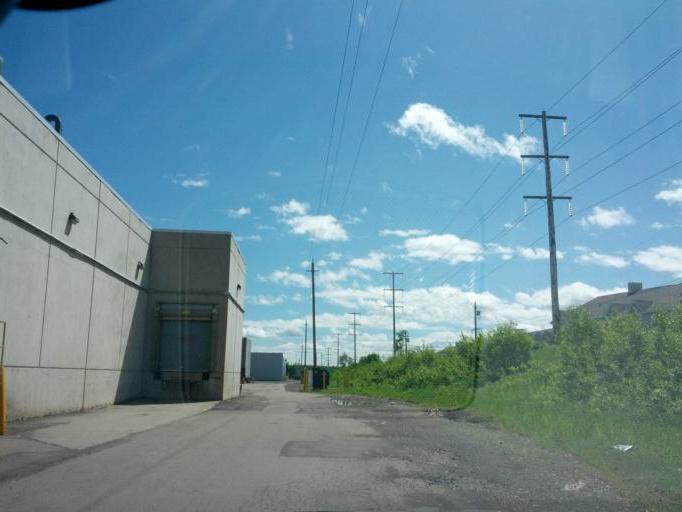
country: CA
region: New Brunswick
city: Moncton
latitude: 46.1178
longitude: -64.8340
